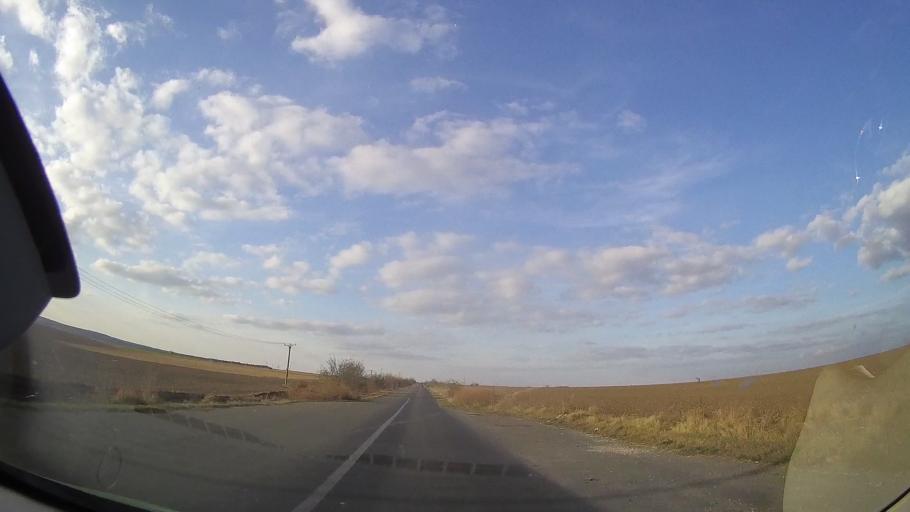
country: RO
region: Constanta
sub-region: Comuna Dumbraveni
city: Dumbraveni
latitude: 43.9291
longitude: 28.0290
